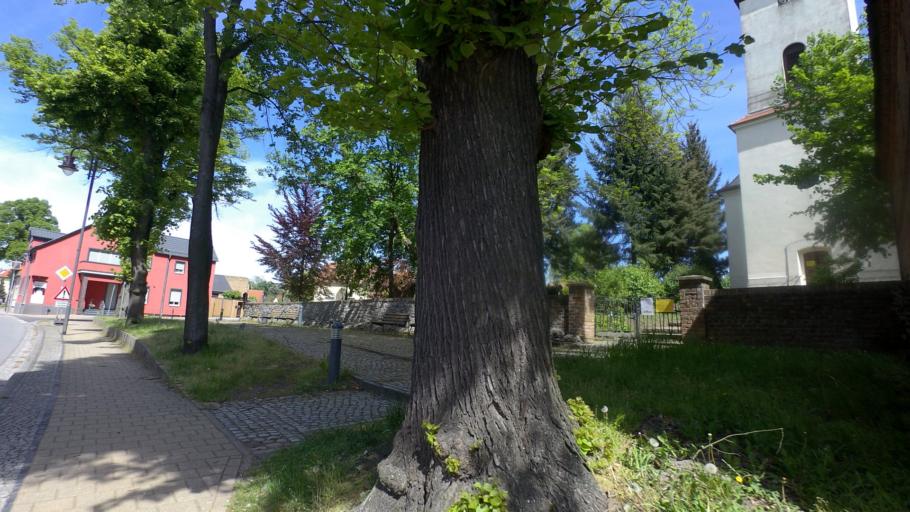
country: DE
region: Brandenburg
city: Sperenberg
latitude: 52.1409
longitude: 13.3652
